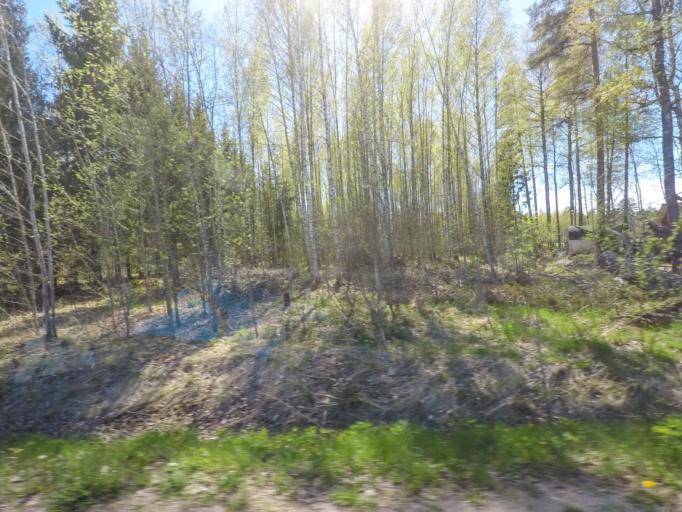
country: FI
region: Uusimaa
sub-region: Helsinki
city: Sammatti
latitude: 60.3341
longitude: 23.8028
